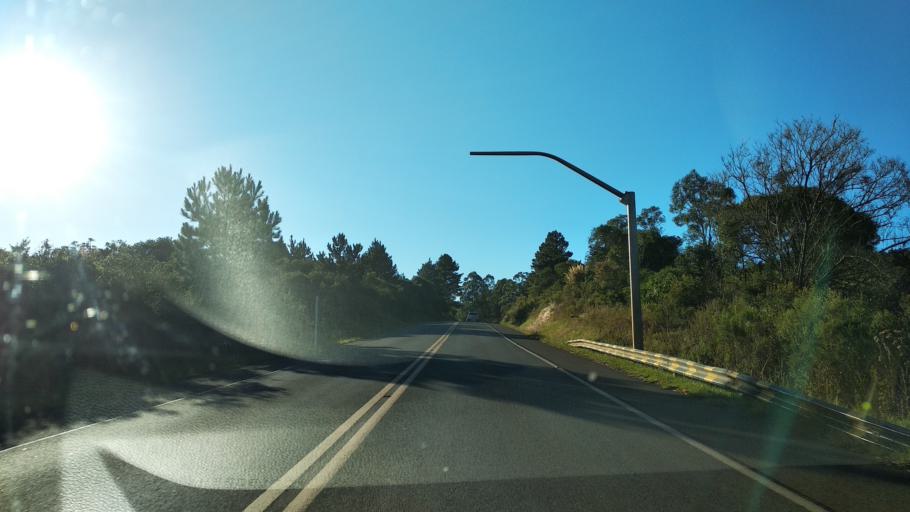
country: BR
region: Santa Catarina
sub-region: Lages
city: Lages
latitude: -27.7853
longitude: -50.4443
